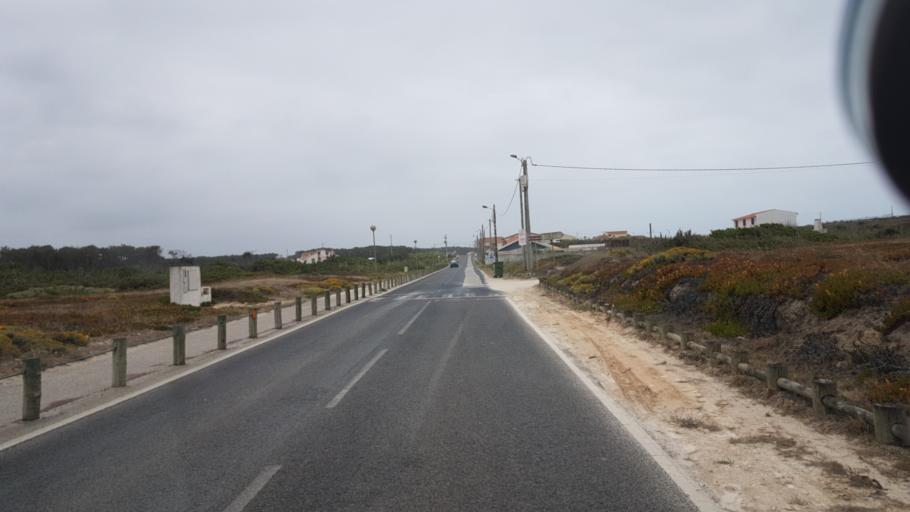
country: PT
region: Lisbon
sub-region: Torres Vedras
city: Silveira
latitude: 39.1645
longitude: -9.3596
